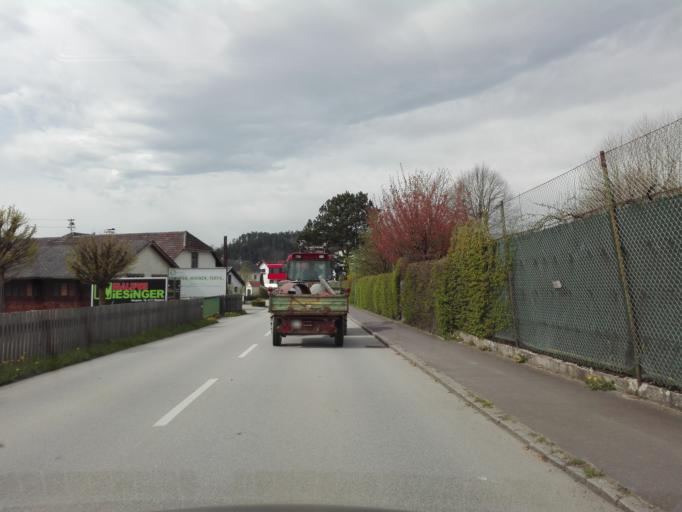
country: AT
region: Upper Austria
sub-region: Politischer Bezirk Urfahr-Umgebung
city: Walding
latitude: 48.3503
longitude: 14.1572
